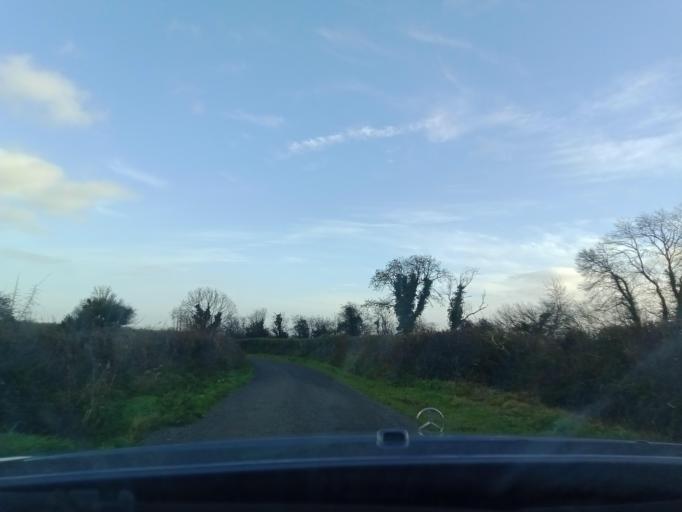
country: IE
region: Leinster
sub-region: Kilkenny
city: Callan
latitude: 52.4704
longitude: -7.3888
